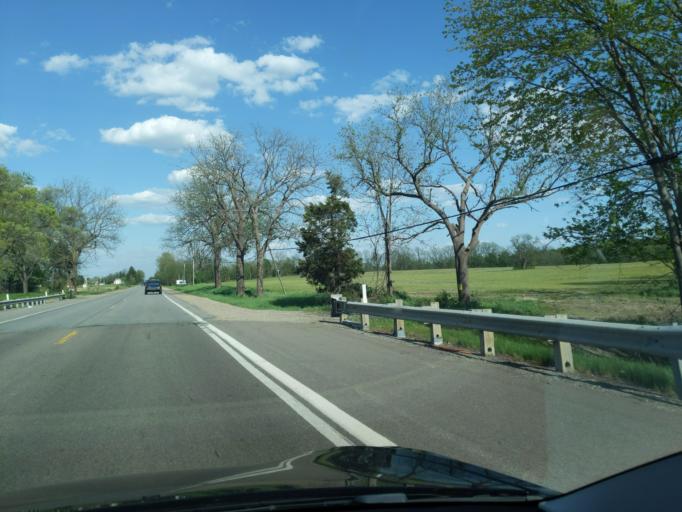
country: US
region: Michigan
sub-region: Eaton County
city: Grand Ledge
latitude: 42.7555
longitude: -84.7941
